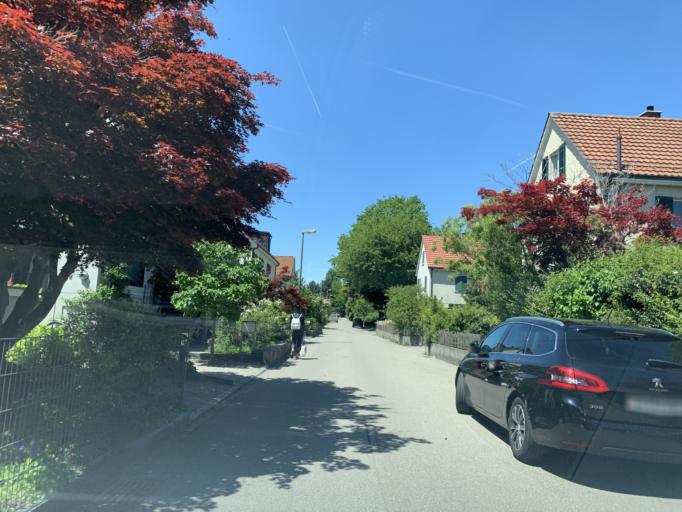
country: CH
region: Zurich
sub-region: Bezirk Winterthur
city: Veltheim (Kreis 5) / Blumenau
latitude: 47.5084
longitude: 8.7106
